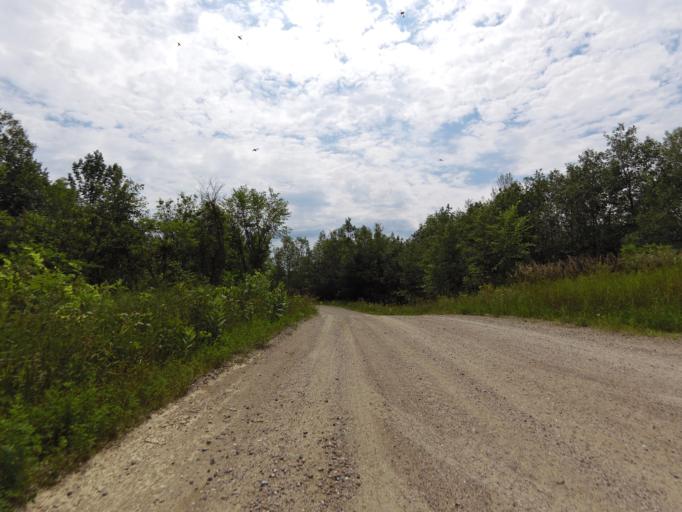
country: CA
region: Ontario
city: Perth
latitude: 44.7409
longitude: -76.6104
